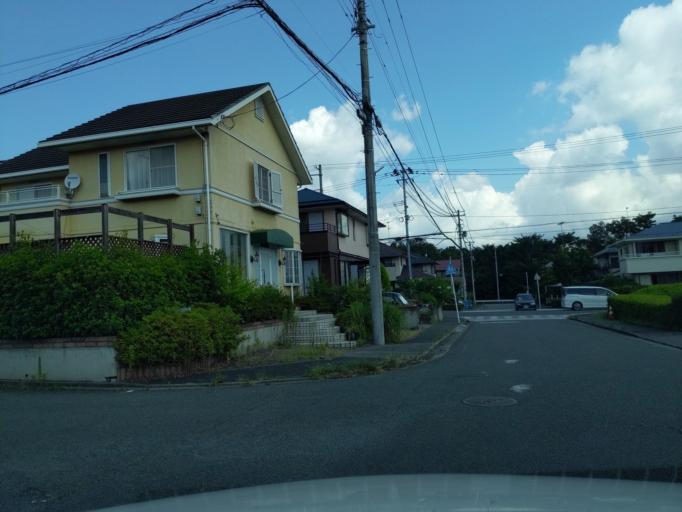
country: JP
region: Fukushima
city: Sukagawa
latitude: 37.3414
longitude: 140.3455
